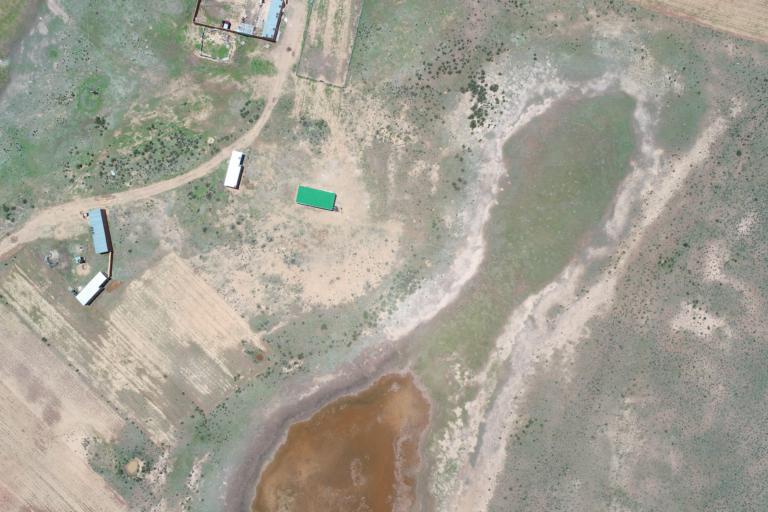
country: BO
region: La Paz
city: Curahuara de Carangas
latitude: -17.2855
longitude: -68.5167
